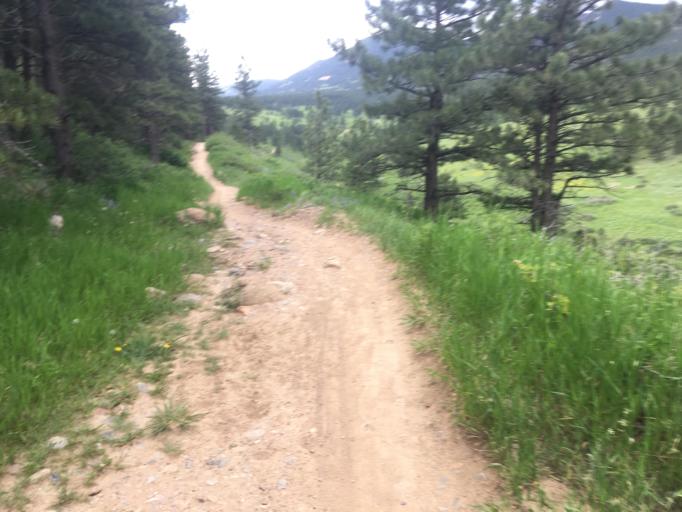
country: US
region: Colorado
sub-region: Boulder County
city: Superior
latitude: 39.9201
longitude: -105.2582
